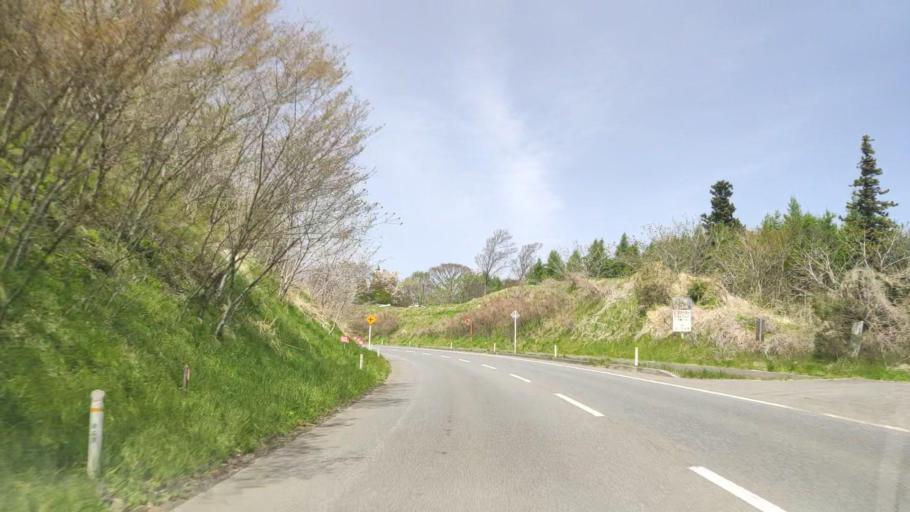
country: JP
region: Aomori
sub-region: Hachinohe Shi
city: Uchimaru
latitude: 40.5201
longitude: 141.4261
